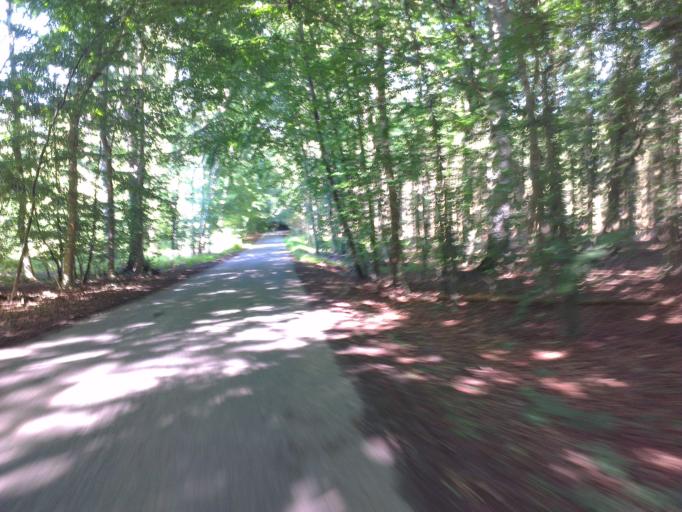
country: DK
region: Capital Region
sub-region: Frederikssund Kommune
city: Skibby
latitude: 55.7180
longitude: 11.9507
